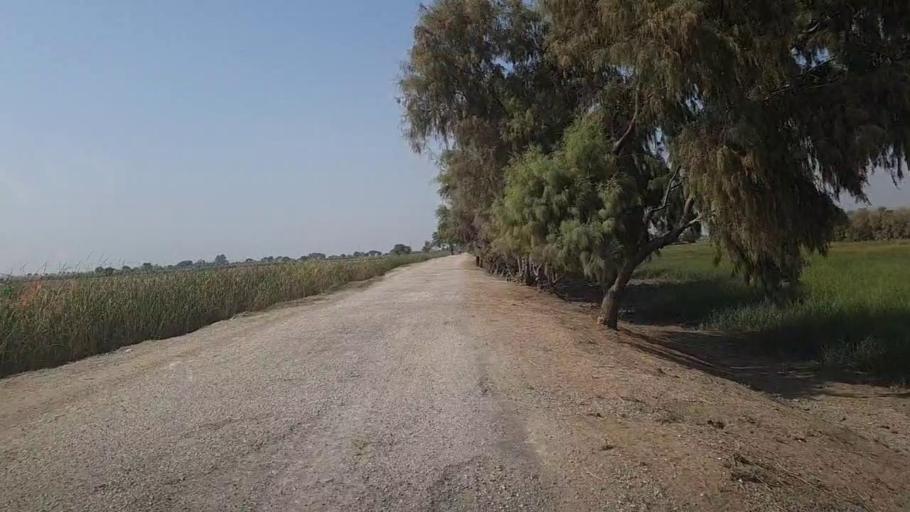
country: PK
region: Sindh
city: Kandhkot
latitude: 28.4029
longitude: 69.2595
